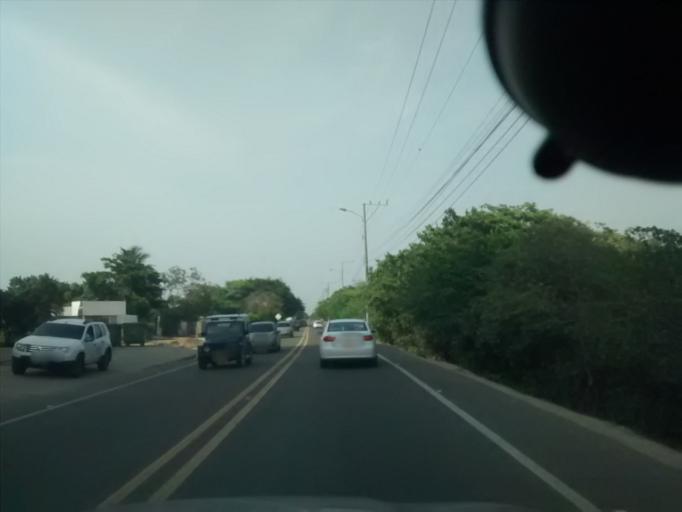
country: CO
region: Bolivar
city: Cartagena
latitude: 10.4673
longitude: -75.4990
